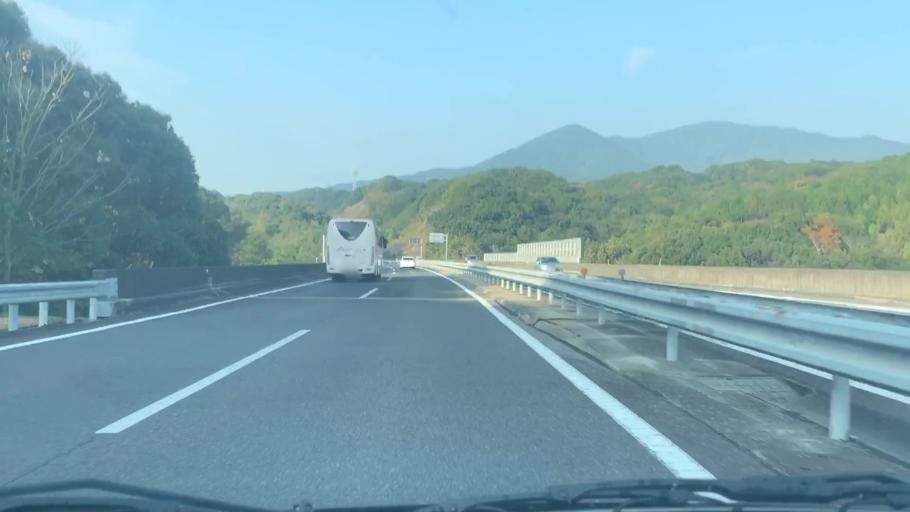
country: JP
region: Saga Prefecture
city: Imaricho-ko
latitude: 33.1699
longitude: 129.8443
